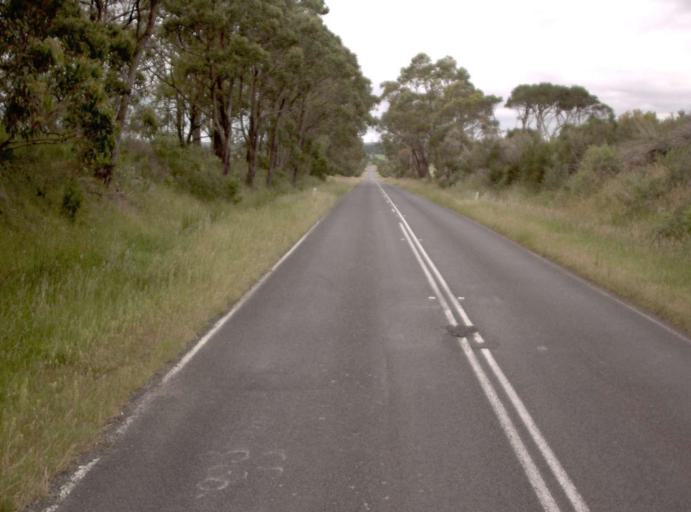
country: AU
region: Victoria
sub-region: Bass Coast
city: North Wonthaggi
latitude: -38.5414
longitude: 145.6978
